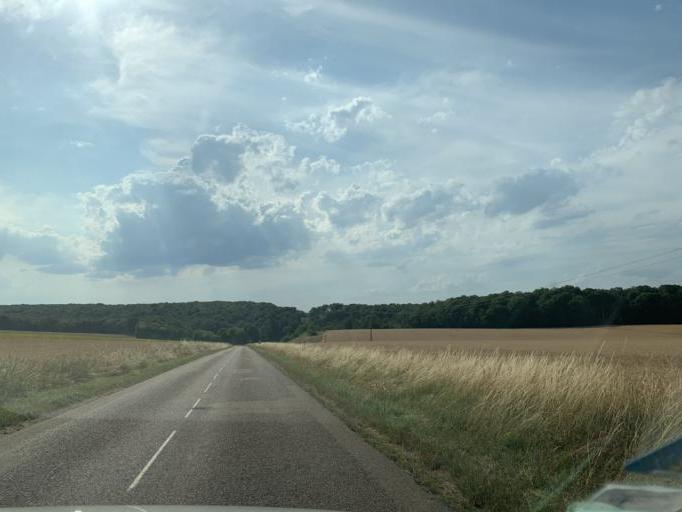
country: FR
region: Bourgogne
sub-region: Departement de l'Yonne
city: Fontenailles
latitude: 47.5184
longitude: 3.4170
